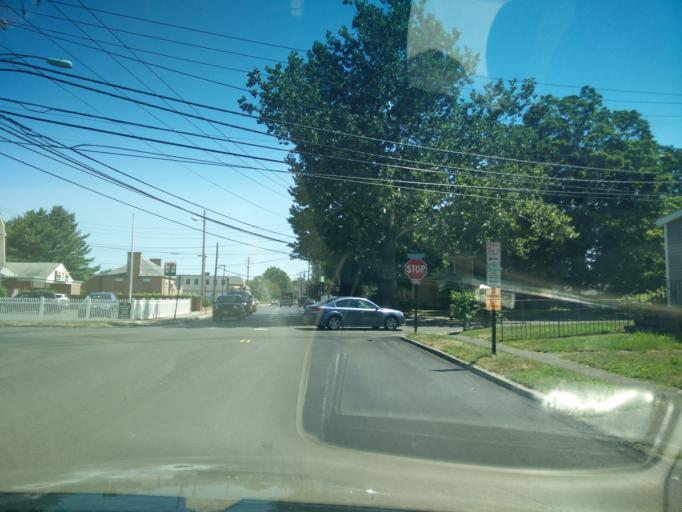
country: US
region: Connecticut
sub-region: Fairfield County
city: Fairfield
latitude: 41.1384
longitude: -73.2558
